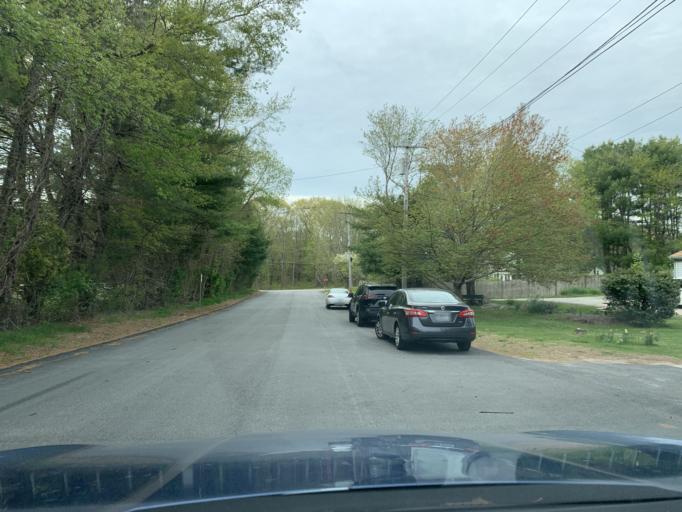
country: US
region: Rhode Island
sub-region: Washington County
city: Exeter
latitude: 41.6221
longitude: -71.5220
